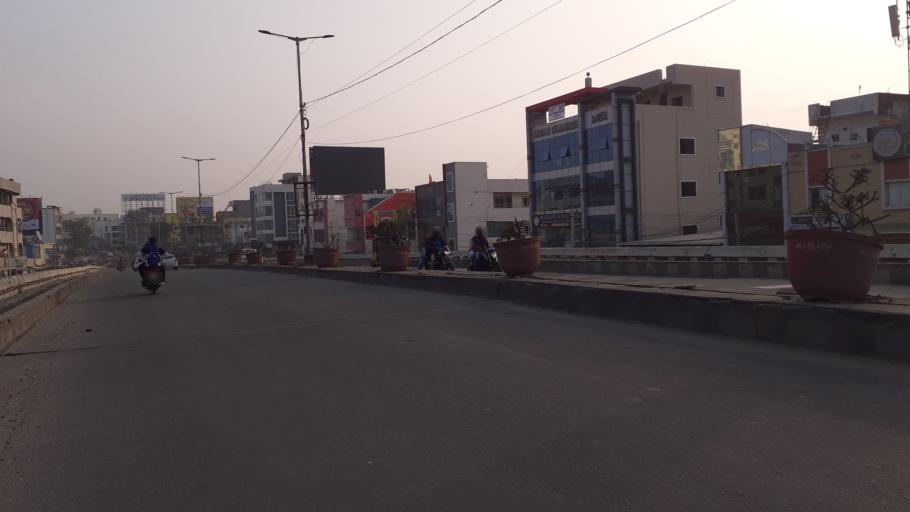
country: IN
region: Telangana
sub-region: Rangareddi
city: Kukatpalli
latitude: 17.4824
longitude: 78.3607
